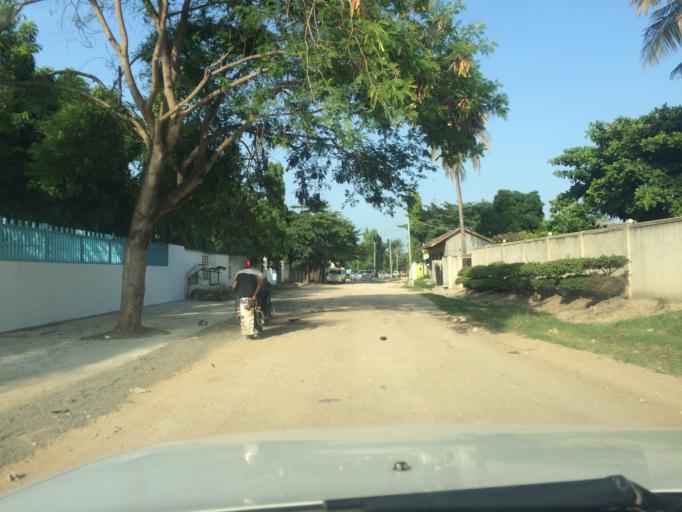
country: TZ
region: Dar es Salaam
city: Magomeni
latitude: -6.7738
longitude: 39.2565
